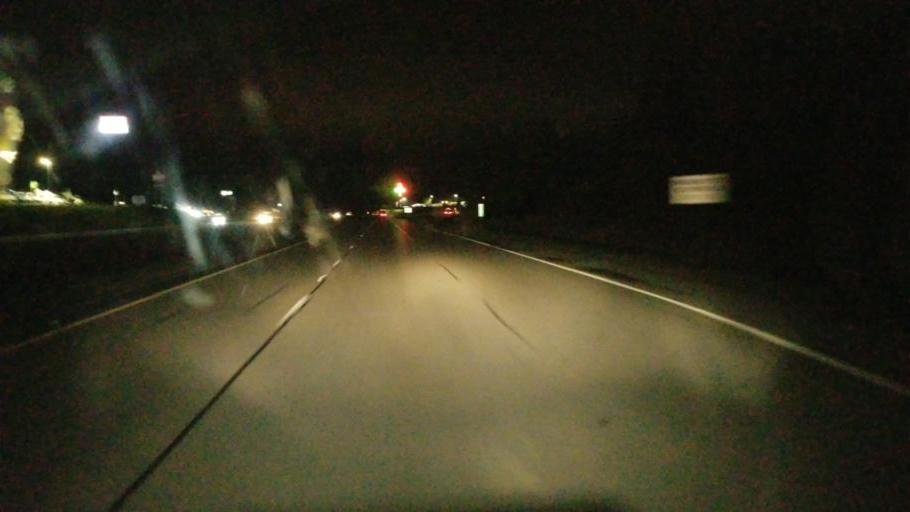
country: US
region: Ohio
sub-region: Muskingum County
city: Pleasant Grove
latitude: 39.9686
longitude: -81.8932
